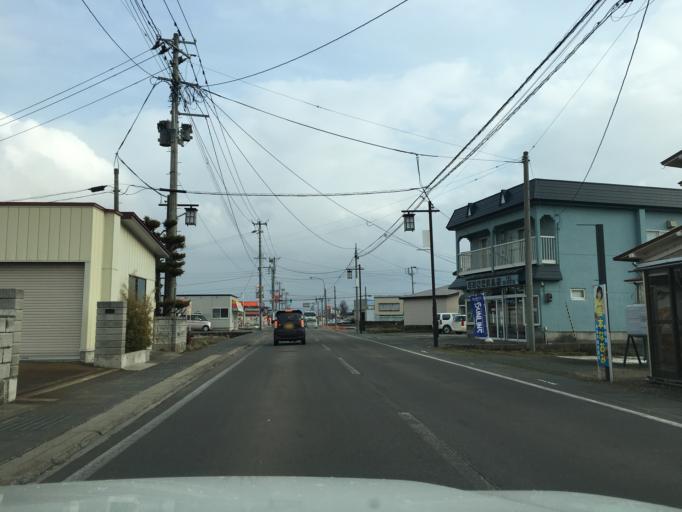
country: JP
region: Aomori
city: Namioka
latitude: 40.7098
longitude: 140.5900
